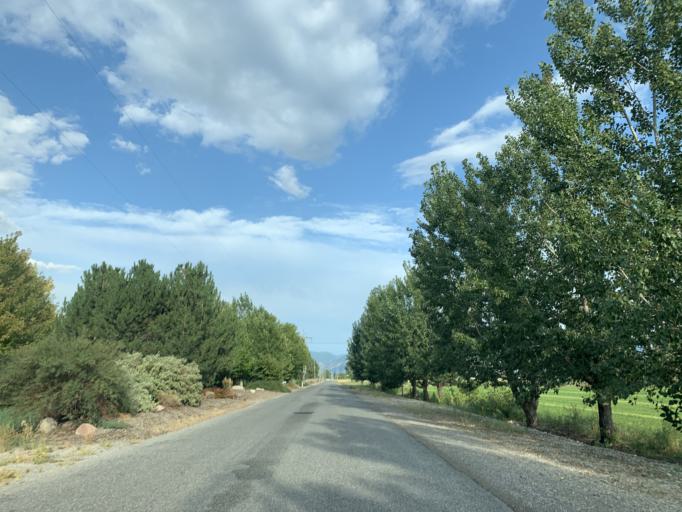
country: US
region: Utah
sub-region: Utah County
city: Benjamin
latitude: 40.1292
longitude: -111.7437
